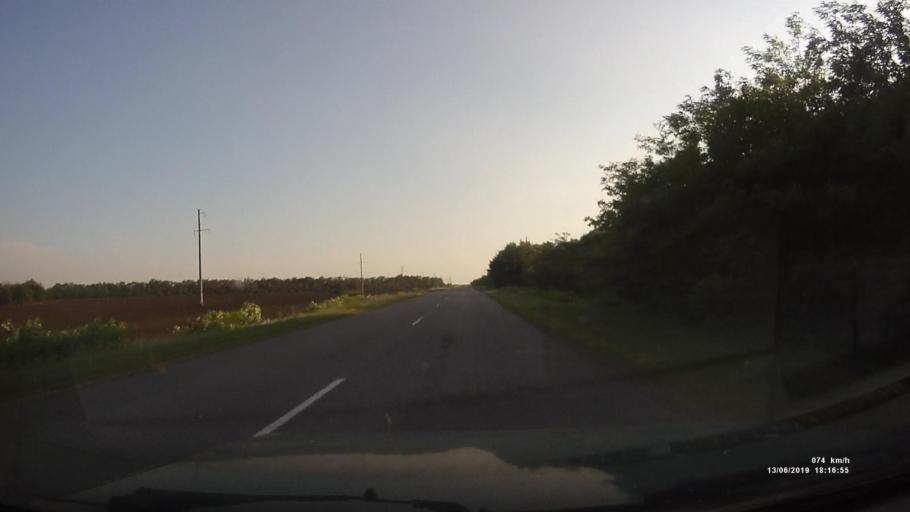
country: RU
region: Rostov
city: Kazanskaya
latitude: 49.9243
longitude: 41.3322
